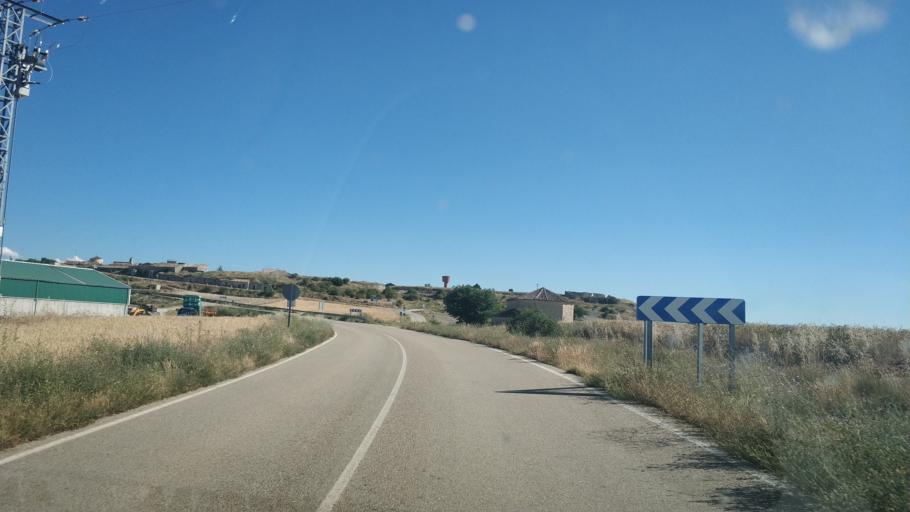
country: ES
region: Castille and Leon
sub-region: Provincia de Soria
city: Liceras
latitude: 41.4687
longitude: -3.2173
